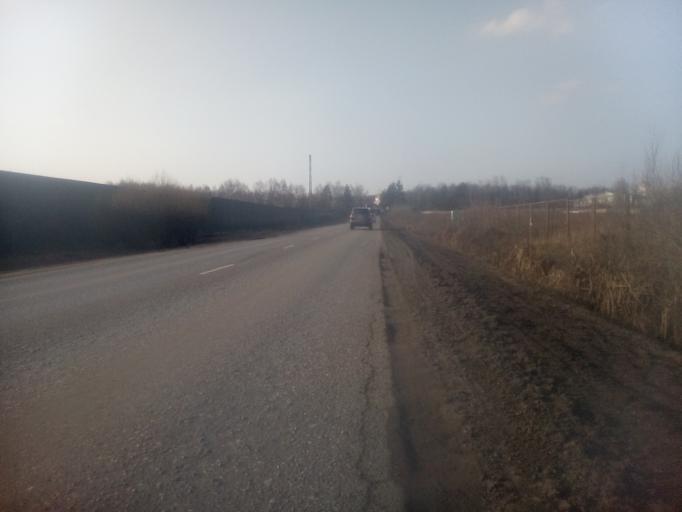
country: RU
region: Moskovskaya
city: Kokoshkino
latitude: 55.6153
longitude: 37.1603
